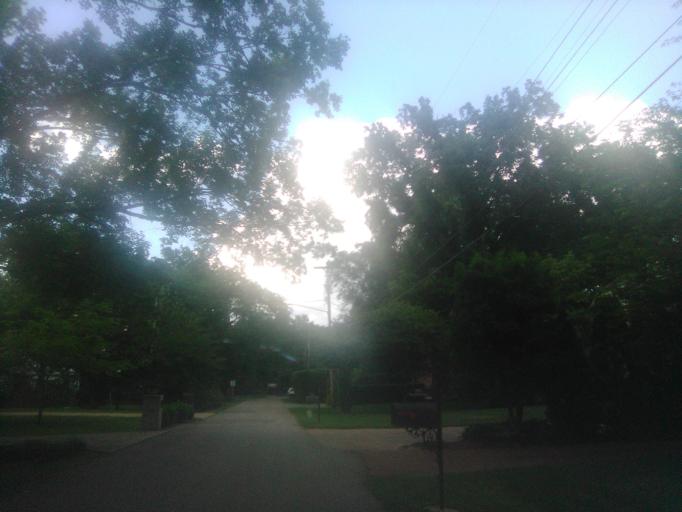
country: US
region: Tennessee
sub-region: Davidson County
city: Belle Meade
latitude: 36.1148
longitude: -86.8288
